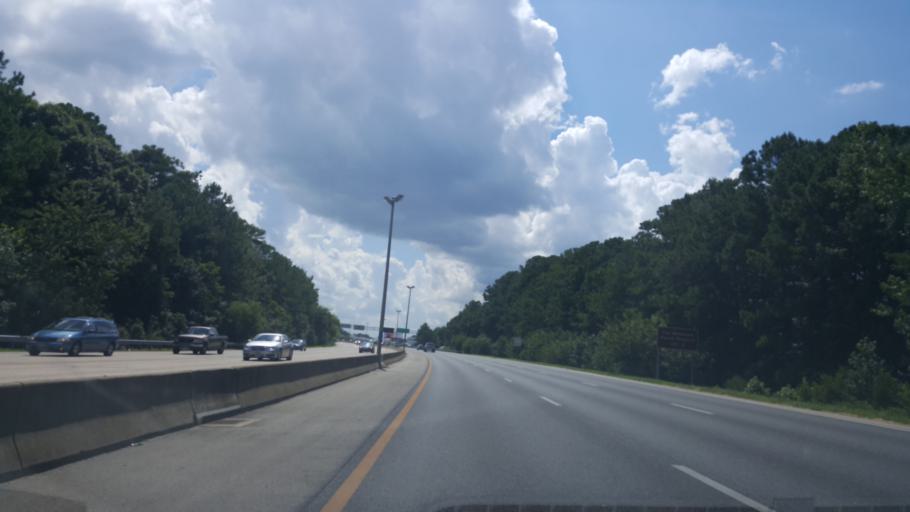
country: US
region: Virginia
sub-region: City of Newport News
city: Newport News
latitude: 37.0129
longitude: -76.3930
